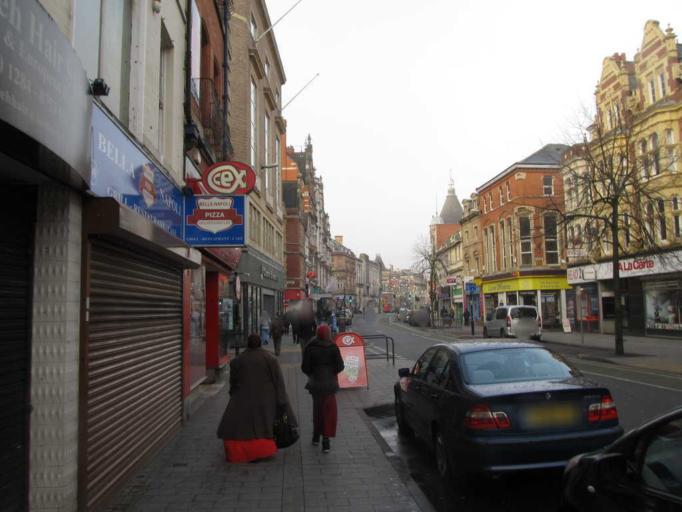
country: GB
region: England
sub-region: City of Leicester
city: Leicester
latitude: 52.6328
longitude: -1.1285
